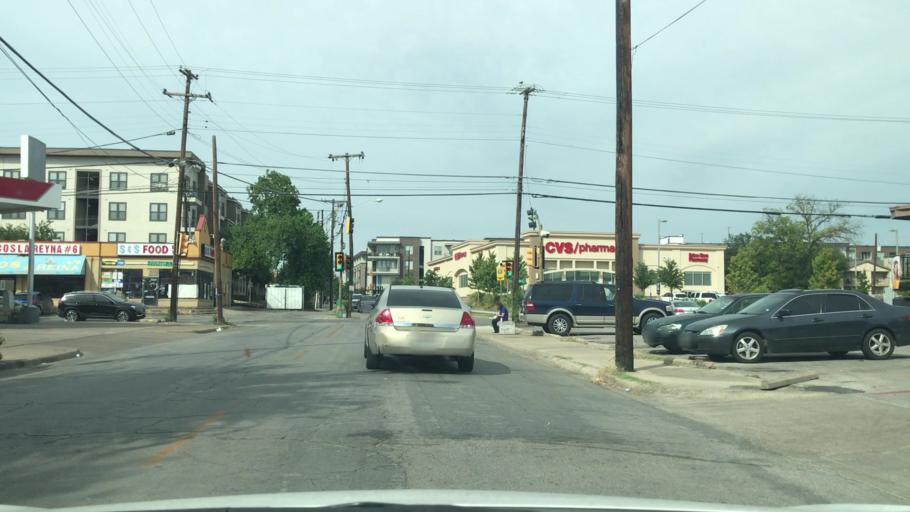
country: US
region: Texas
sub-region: Dallas County
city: Highland Park
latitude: 32.8109
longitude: -96.7825
